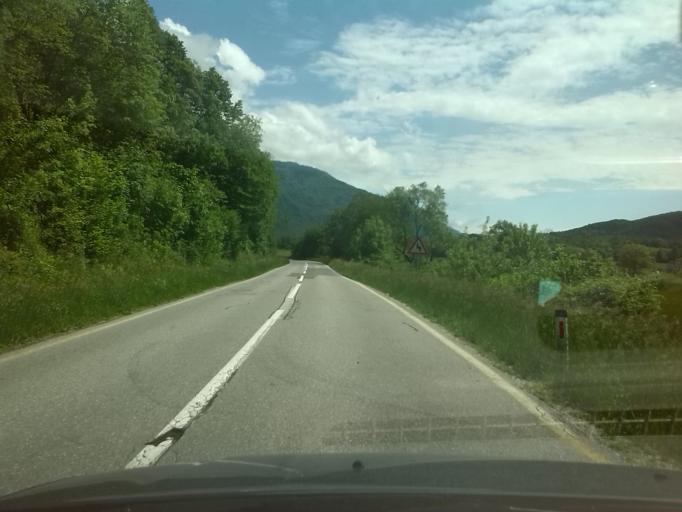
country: SI
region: Kobarid
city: Kobarid
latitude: 46.2473
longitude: 13.5475
